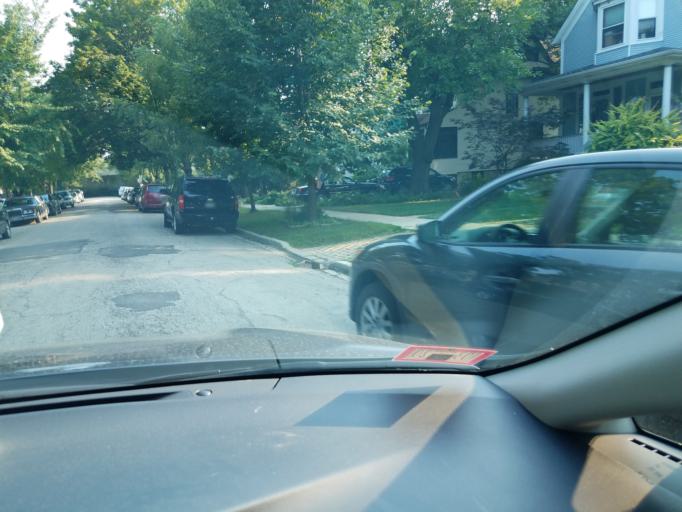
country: US
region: Illinois
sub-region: Cook County
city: Lincolnwood
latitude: 41.9581
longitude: -87.7356
